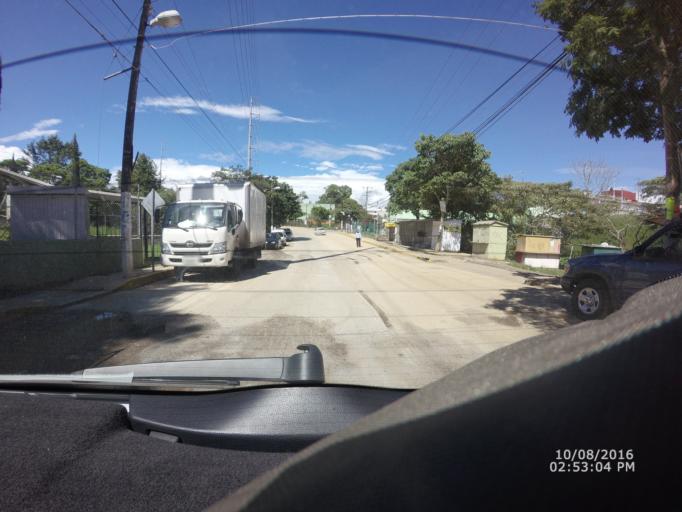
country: MX
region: Veracruz
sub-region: Xalapa
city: Colonia Santa Barbara
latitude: 19.5027
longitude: -96.8783
